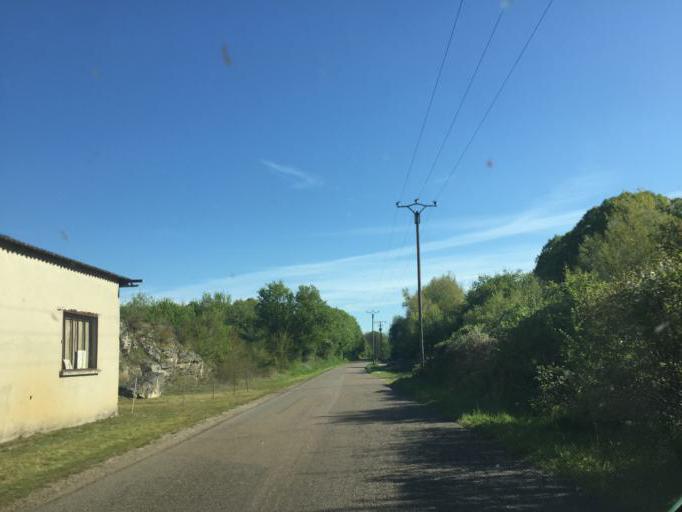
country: FR
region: Bourgogne
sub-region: Departement de la Nievre
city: Clamecy
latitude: 47.5016
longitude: 3.5126
